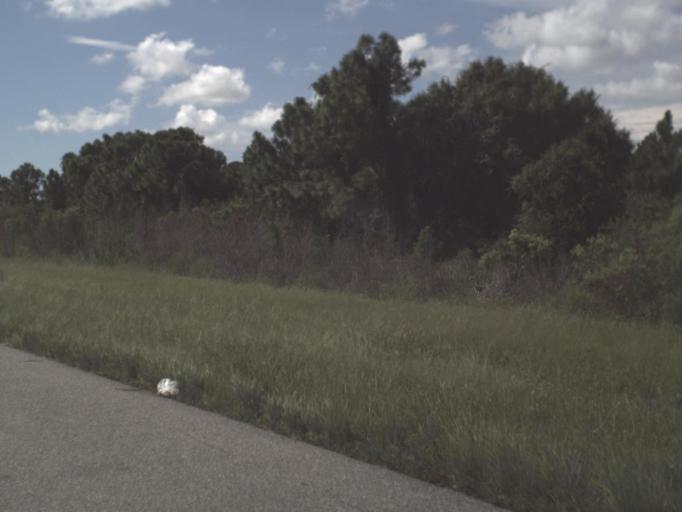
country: US
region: Florida
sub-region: Charlotte County
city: Harbour Heights
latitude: 26.9893
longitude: -82.0299
